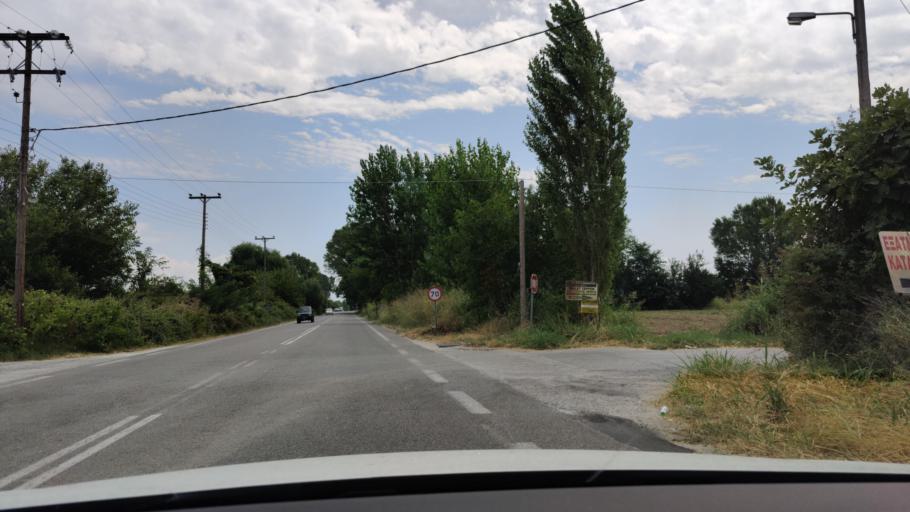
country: GR
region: Central Macedonia
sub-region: Nomos Serron
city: Serres
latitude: 41.0699
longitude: 23.5600
